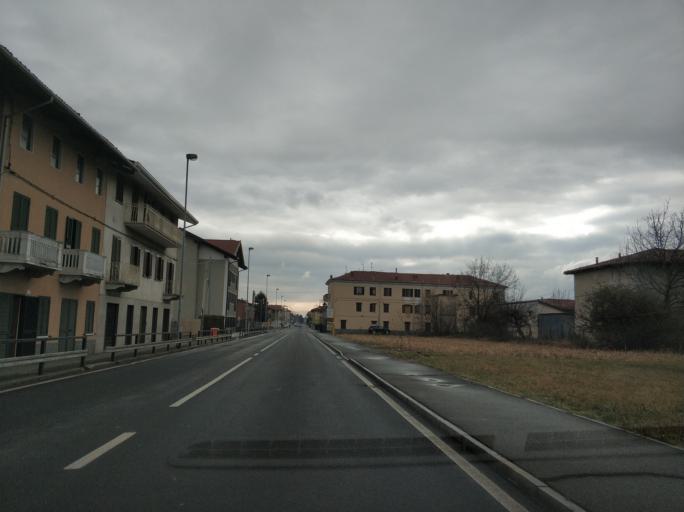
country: IT
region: Piedmont
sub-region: Provincia di Torino
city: Pavone Canavese
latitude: 45.4393
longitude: 7.8783
